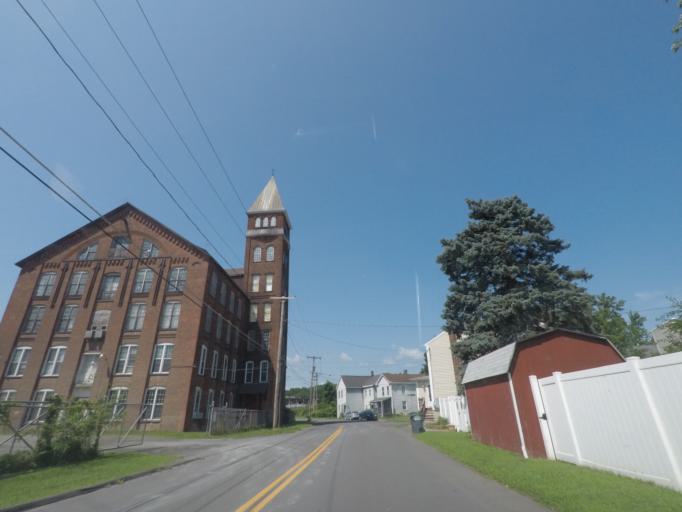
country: US
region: New York
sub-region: Saratoga County
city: Waterford
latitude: 42.7889
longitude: -73.6825
